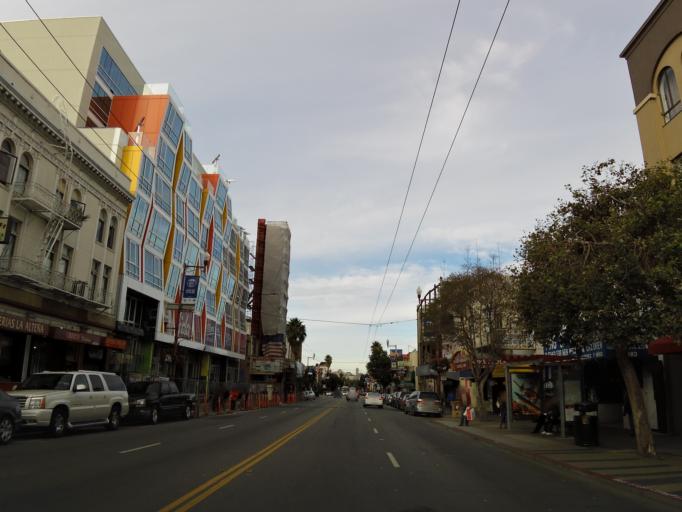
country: US
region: California
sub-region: San Francisco County
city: San Francisco
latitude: 37.7555
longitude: -122.4188
